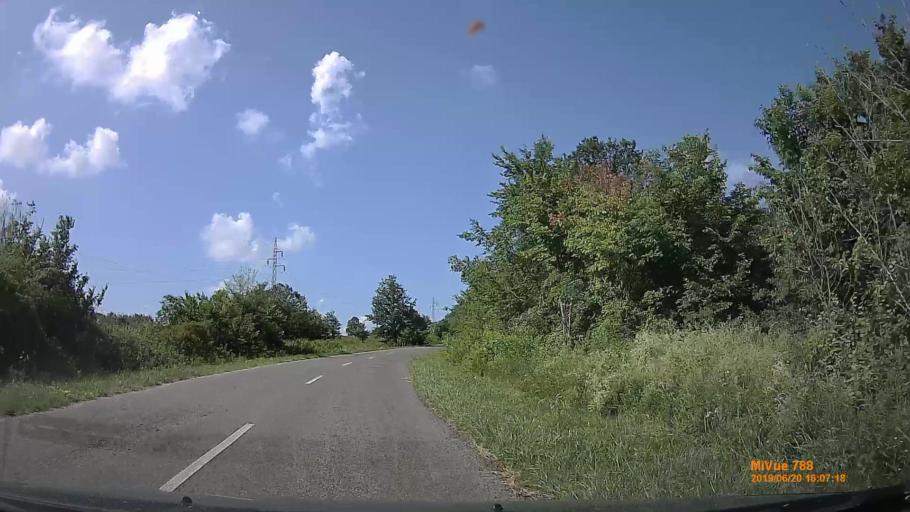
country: HU
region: Baranya
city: Pellerd
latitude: 46.0862
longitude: 18.1111
